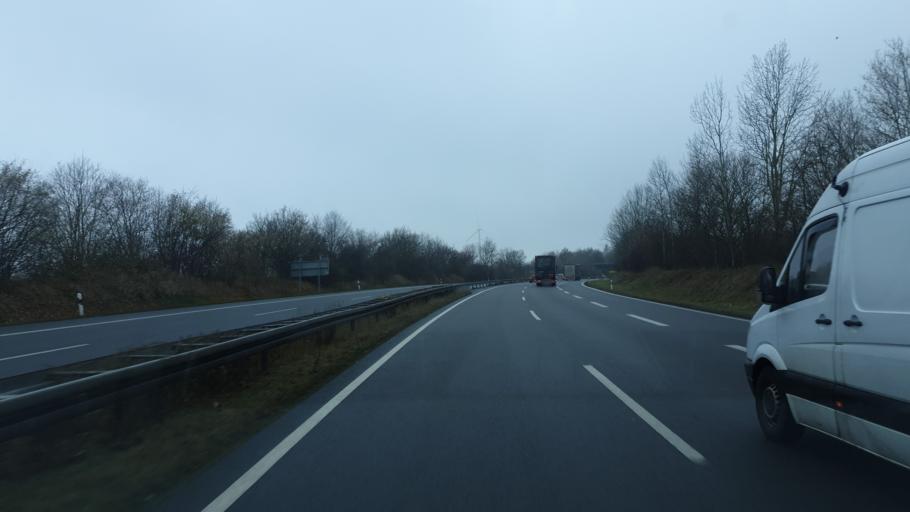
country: DE
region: Saxony
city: Gornau
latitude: 50.7487
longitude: 13.0438
